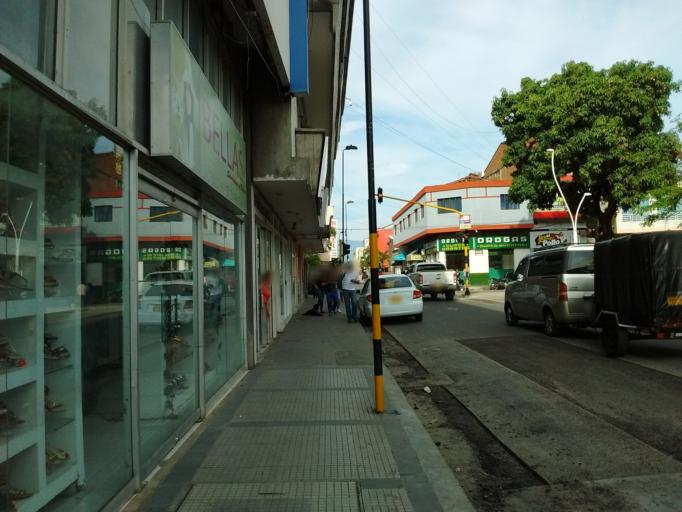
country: CO
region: Valle del Cauca
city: Tulua
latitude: 4.0840
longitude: -76.1959
